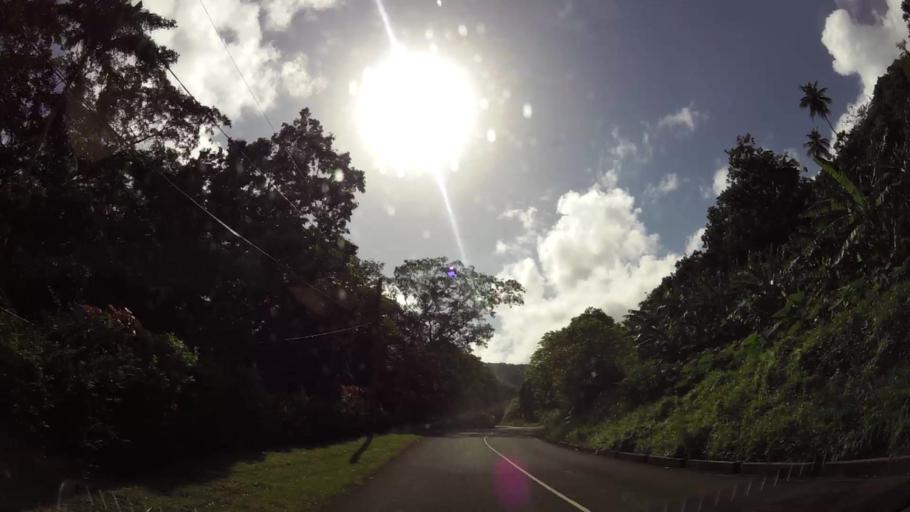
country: DM
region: Saint Andrew
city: Marigot
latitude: 15.5143
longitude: -61.2781
